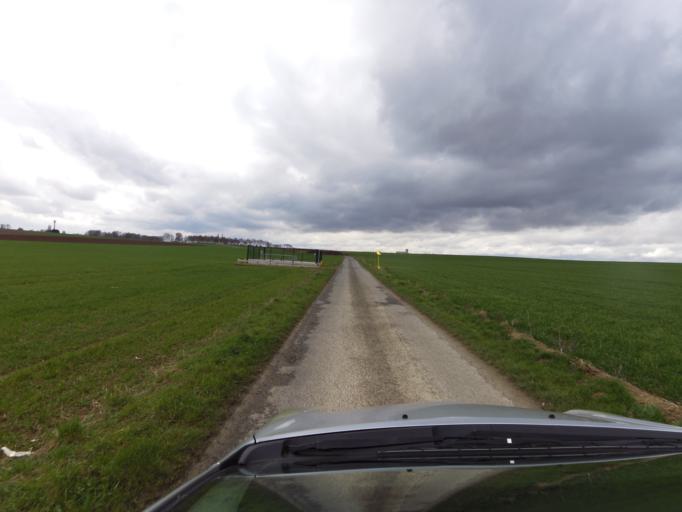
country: FR
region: Nord-Pas-de-Calais
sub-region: Departement du Pas-de-Calais
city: Beaurains
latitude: 50.2216
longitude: 2.7860
